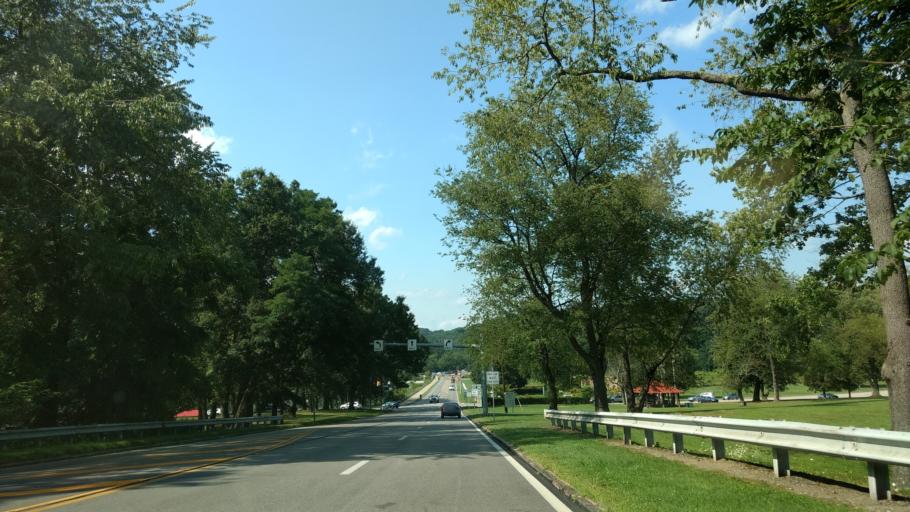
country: US
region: Pennsylvania
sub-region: Allegheny County
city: Gibsonia
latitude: 40.5925
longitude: -79.9969
